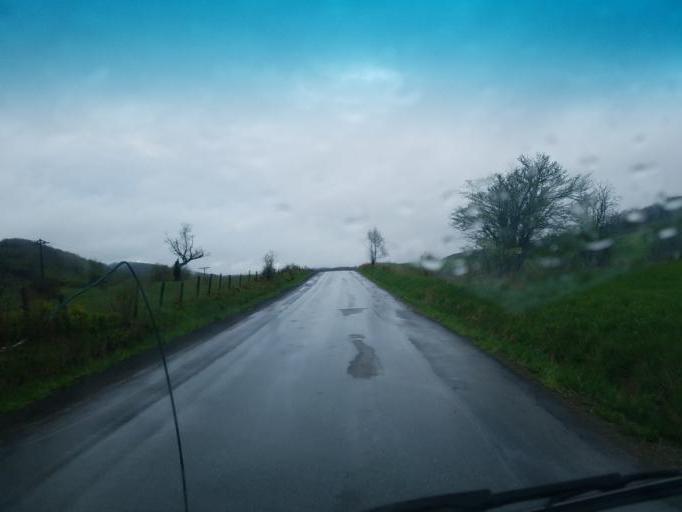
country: US
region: Pennsylvania
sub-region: Tioga County
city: Westfield
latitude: 41.9642
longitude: -77.6510
